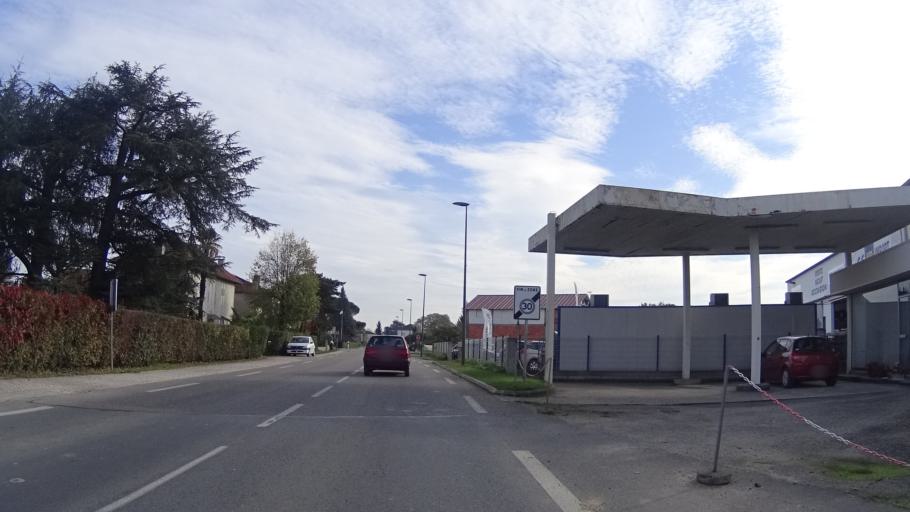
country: FR
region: Aquitaine
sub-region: Departement du Lot-et-Garonne
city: Sainte-Colombe-en-Bruilhois
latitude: 44.2127
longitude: 0.4863
